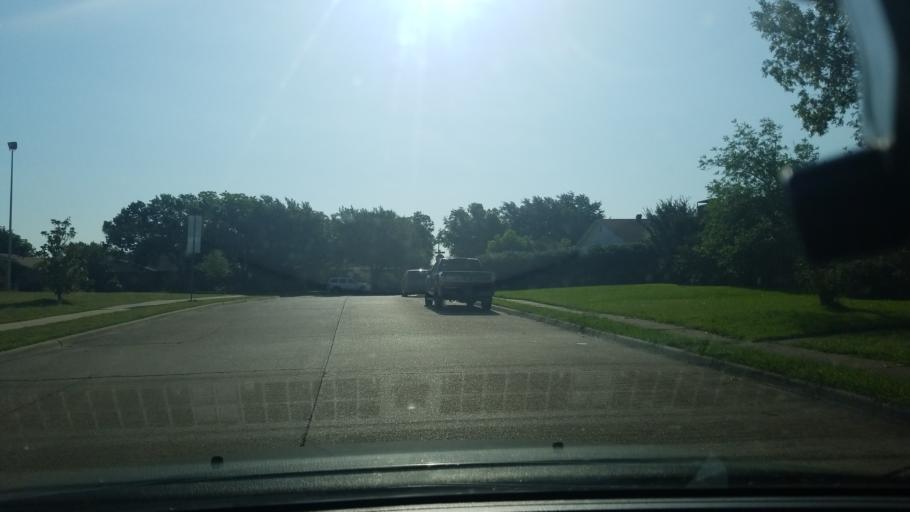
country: US
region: Texas
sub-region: Dallas County
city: Mesquite
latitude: 32.8287
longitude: -96.6359
